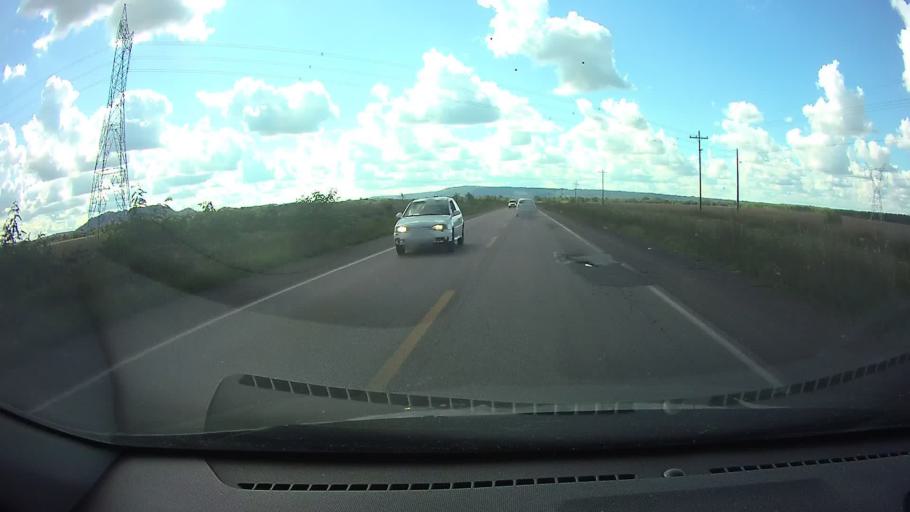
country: PY
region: Paraguari
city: Sapucai
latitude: -25.7263
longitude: -56.8253
